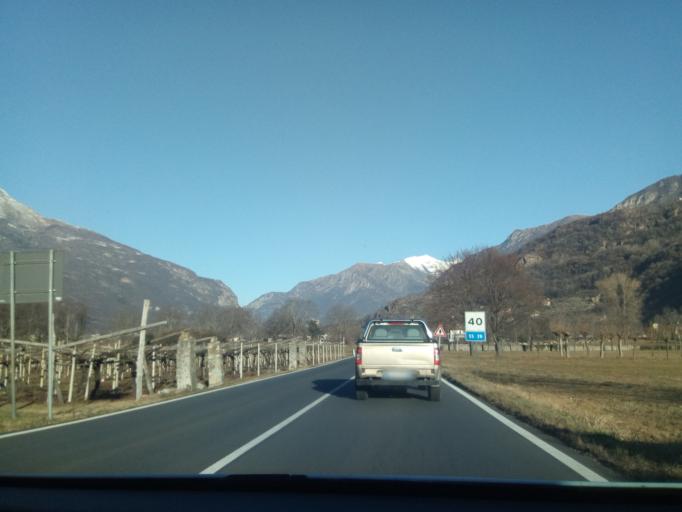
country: IT
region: Piedmont
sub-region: Provincia di Torino
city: Borgofranco d'Ivrea
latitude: 45.5265
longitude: 7.8500
